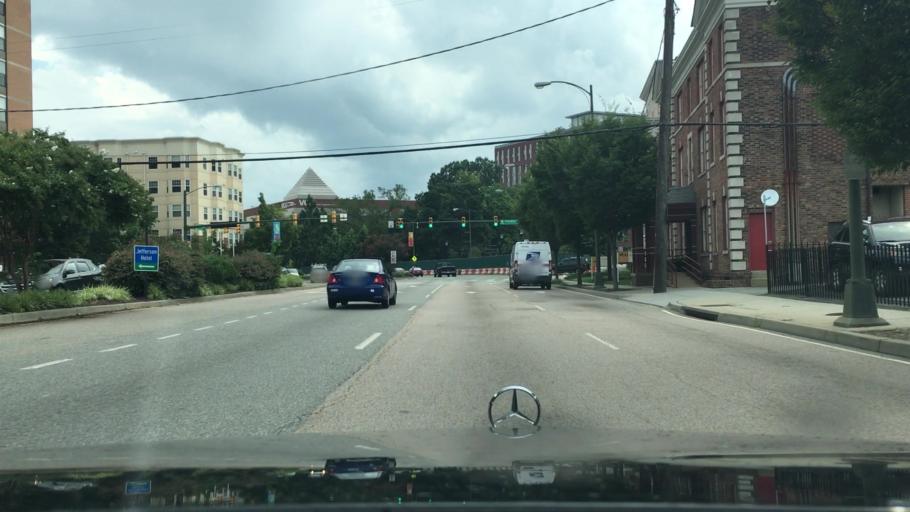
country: US
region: Virginia
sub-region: City of Richmond
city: Richmond
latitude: 37.5477
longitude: -77.4484
